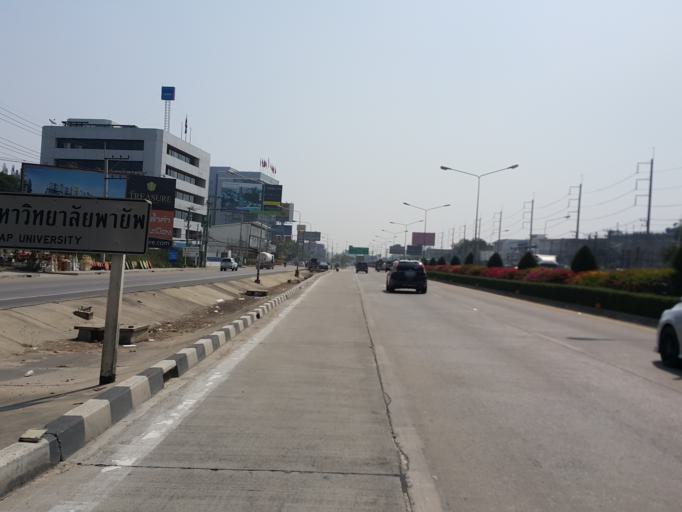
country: TH
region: Chiang Mai
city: Chiang Mai
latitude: 18.8000
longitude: 99.0200
